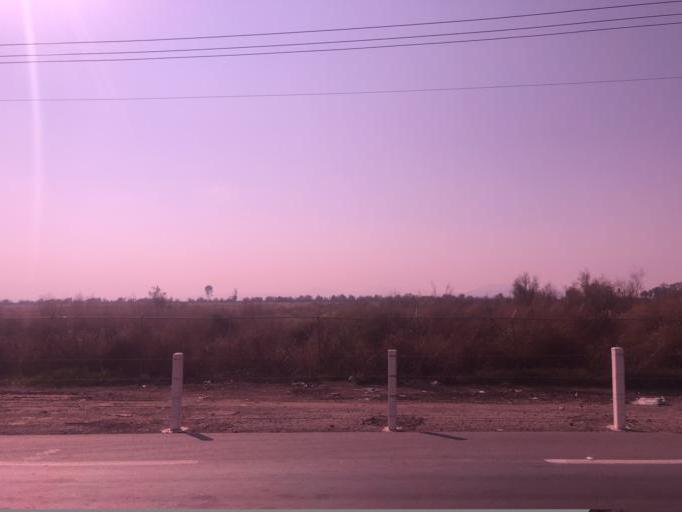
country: MX
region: Mexico
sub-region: Texcoco
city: Colonia Guadalupe Victoria
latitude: 19.4815
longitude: -98.9703
